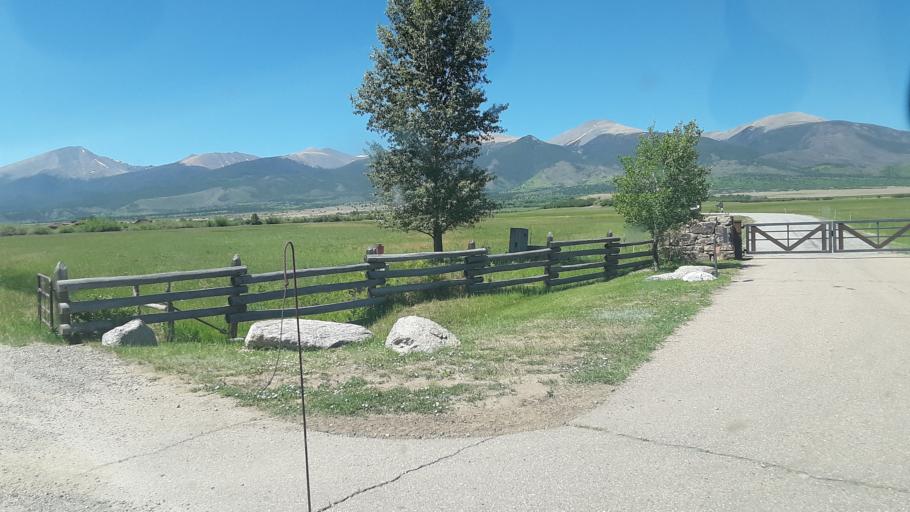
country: US
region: Colorado
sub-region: Custer County
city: Westcliffe
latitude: 38.2897
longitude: -105.6204
